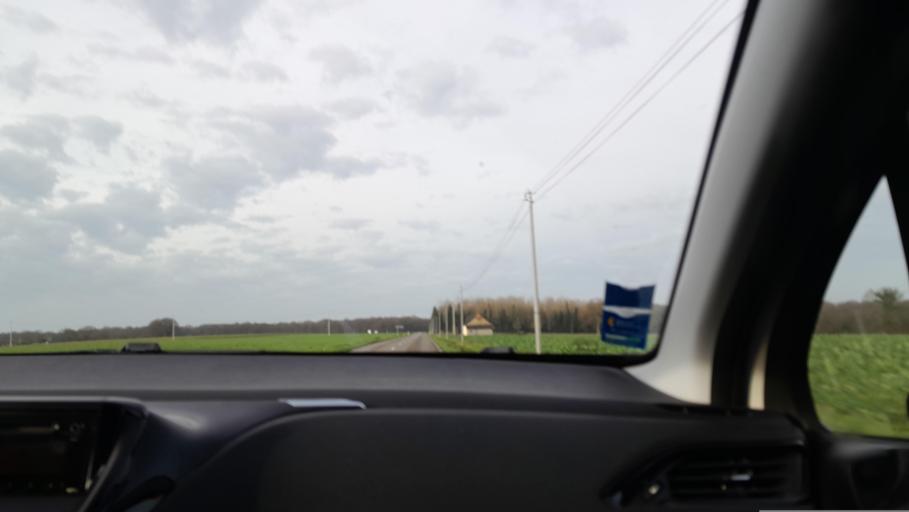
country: FR
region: Brittany
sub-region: Departement d'Ille-et-Vilaine
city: La Guerche-de-Bretagne
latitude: 47.9016
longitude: -1.1687
